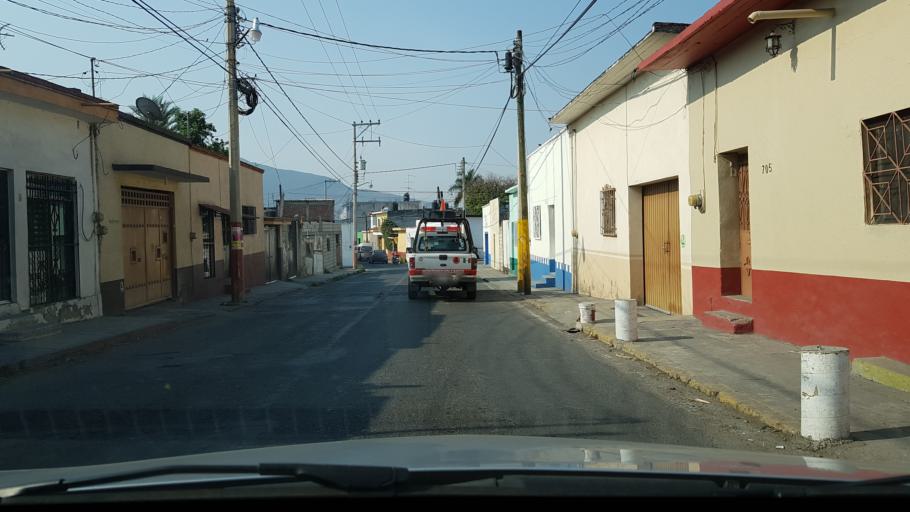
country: MX
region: Morelos
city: Tlaquiltenango
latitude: 18.6337
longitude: -99.1620
